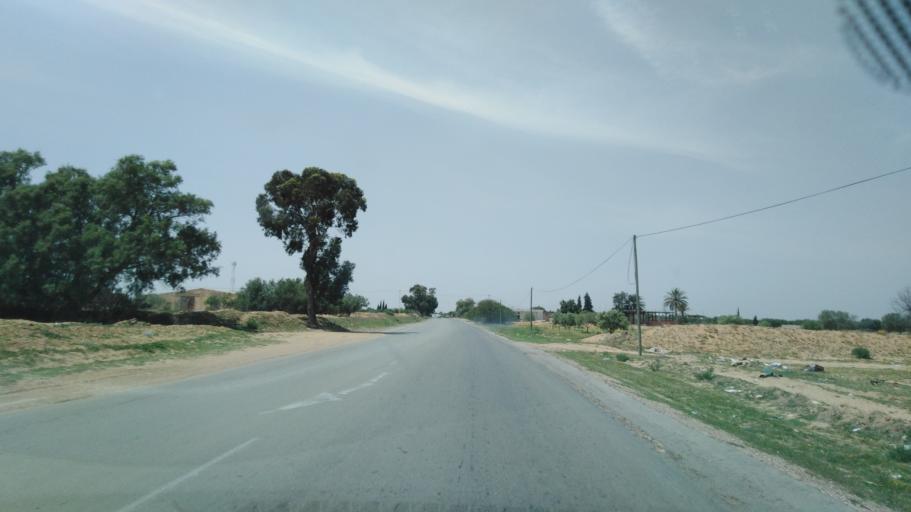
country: TN
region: Safaqis
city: Sfax
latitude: 34.7312
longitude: 10.5632
